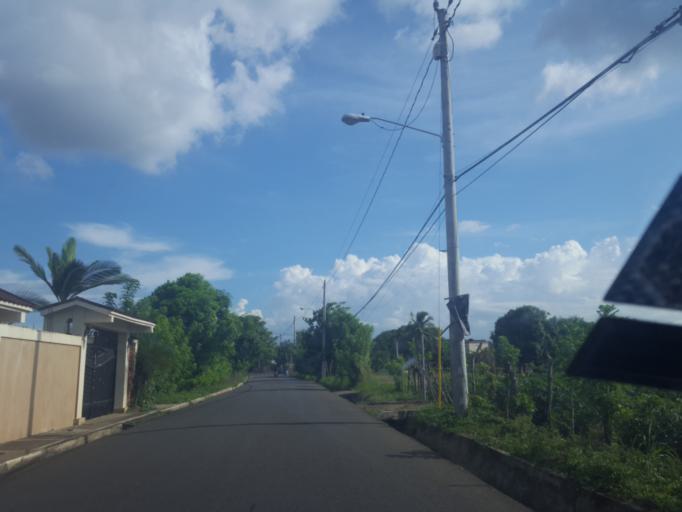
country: DO
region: Santiago
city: Licey al Medio
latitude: 19.3780
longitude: -70.6231
